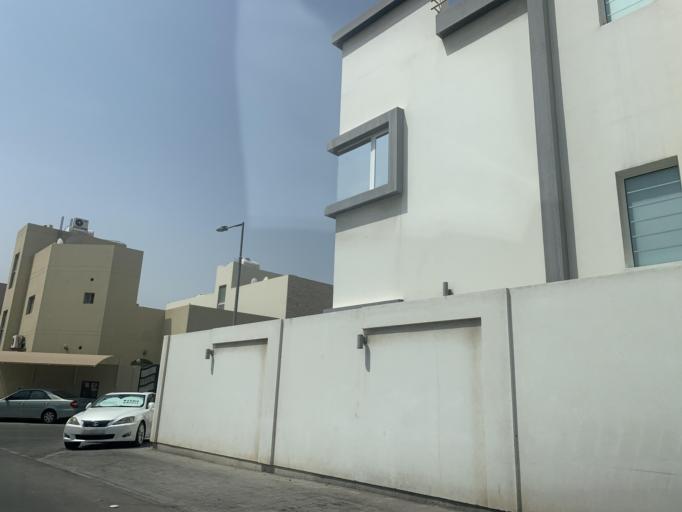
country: BH
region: Manama
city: Jidd Hafs
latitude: 26.2090
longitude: 50.5064
